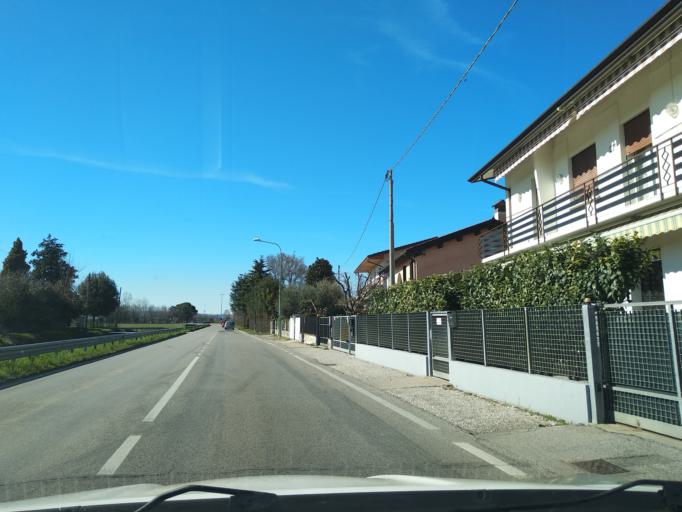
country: IT
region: Veneto
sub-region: Provincia di Padova
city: Caselle
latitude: 45.4129
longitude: 11.8072
